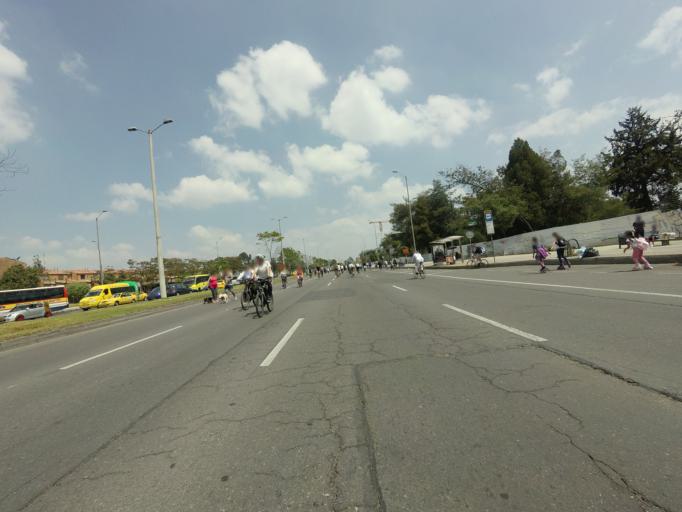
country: CO
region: Bogota D.C.
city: Barrio San Luis
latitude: 4.7306
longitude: -74.0681
